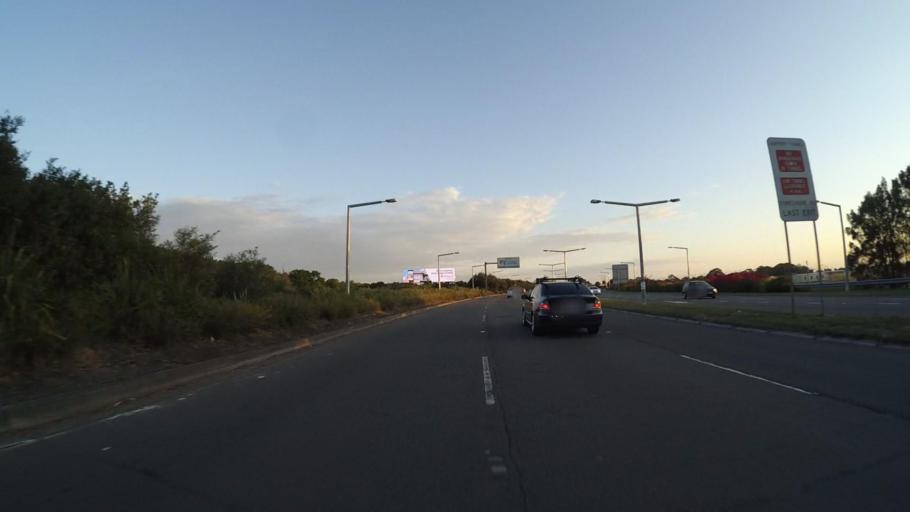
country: AU
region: New South Wales
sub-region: Botany Bay
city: Mascot
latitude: -33.9349
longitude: 151.1926
